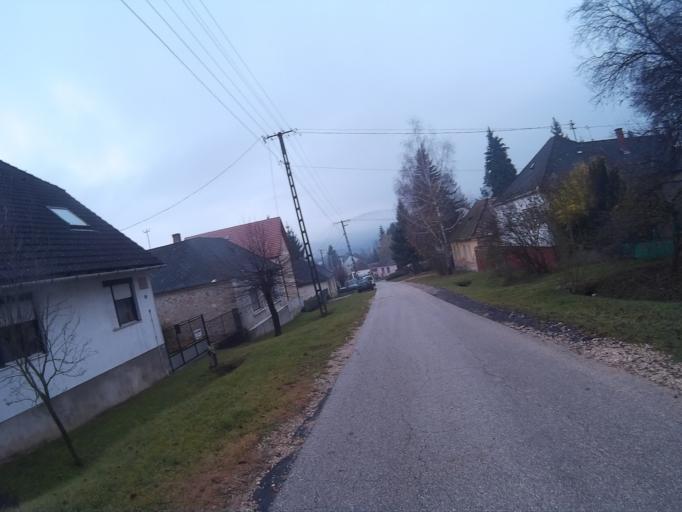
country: HU
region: Veszprem
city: Herend
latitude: 47.2553
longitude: 17.7329
